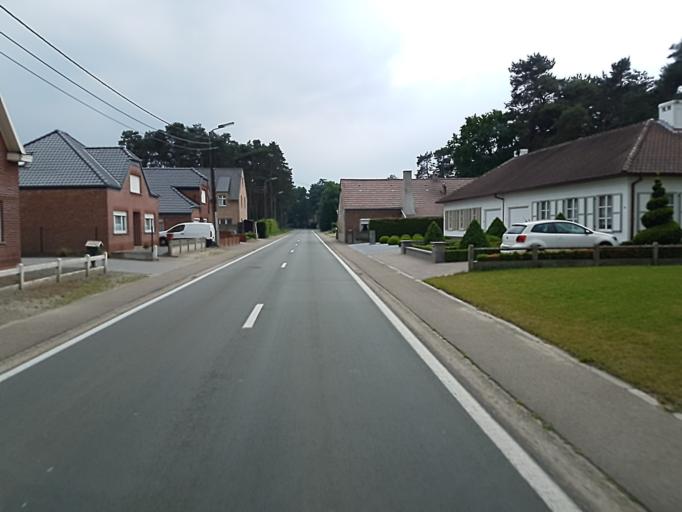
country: BE
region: Flanders
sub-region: Provincie Vlaams-Brabant
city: Tremelo
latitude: 51.0028
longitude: 4.6872
